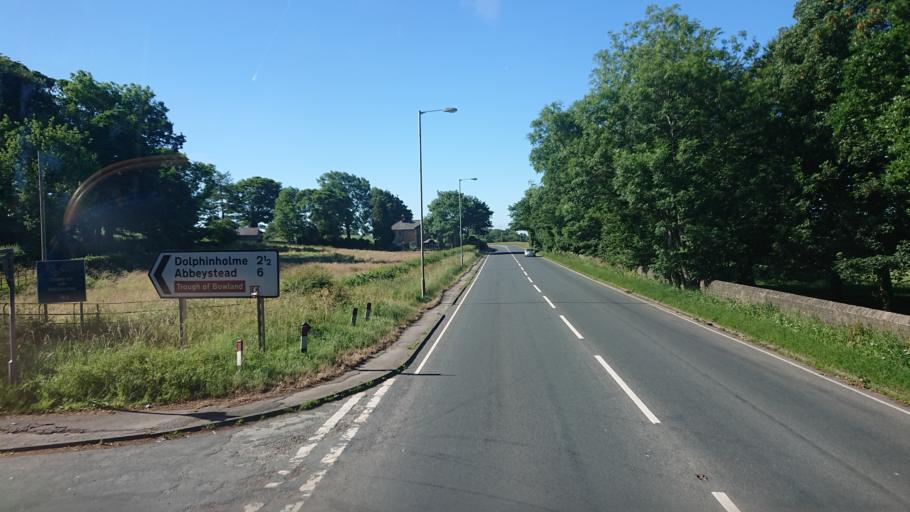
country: GB
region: England
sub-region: Lancashire
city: Galgate
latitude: 53.9783
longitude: -2.7849
